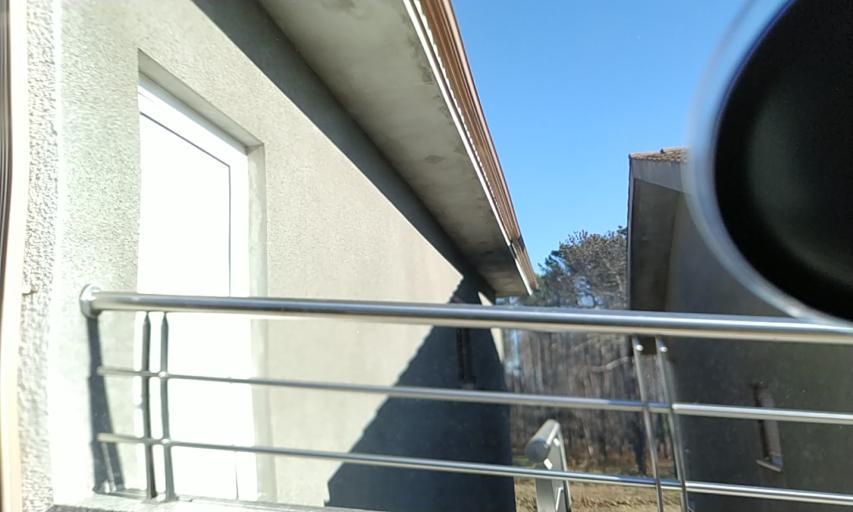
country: PT
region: Vila Real
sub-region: Vila Real
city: Vila Real
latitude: 41.3320
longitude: -7.7566
